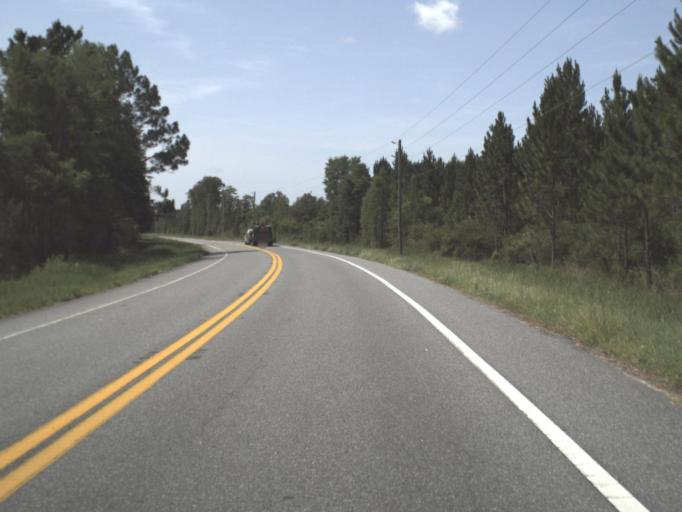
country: US
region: Florida
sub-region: Lafayette County
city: Mayo
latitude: 30.0176
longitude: -83.1944
